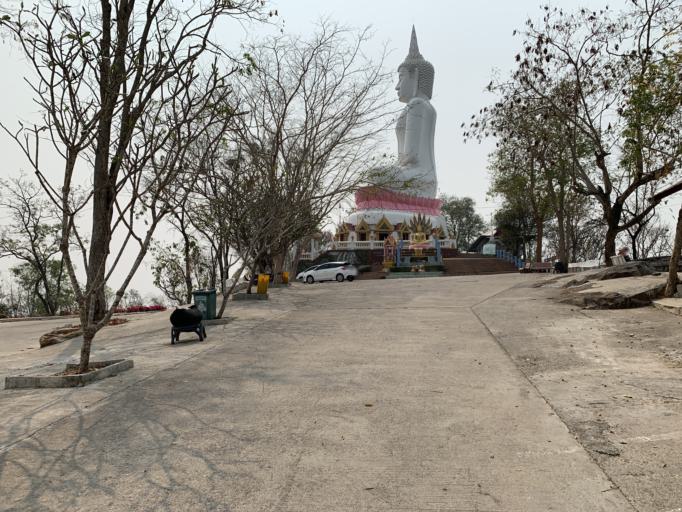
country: TH
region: Khon Kaen
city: Khuean Ubonrat
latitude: 16.7640
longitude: 102.6194
